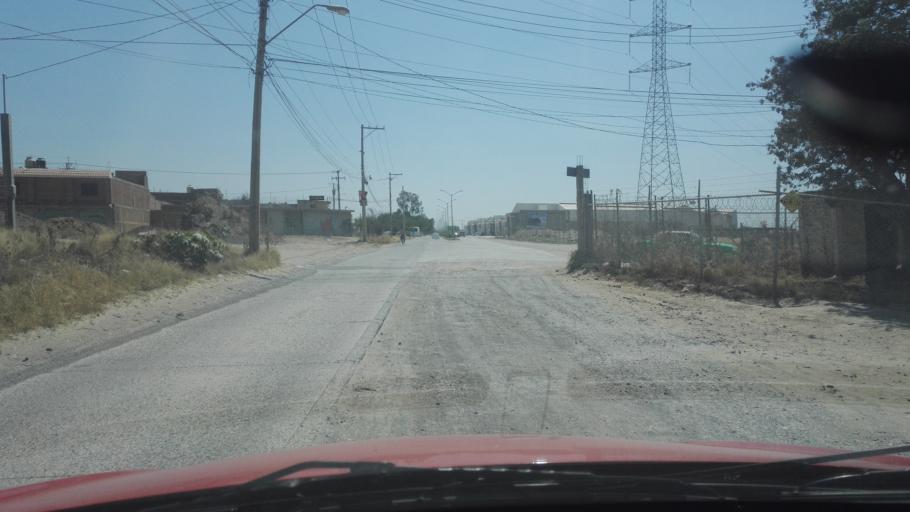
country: MX
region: Guanajuato
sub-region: Leon
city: Fraccionamiento Paraiso Real
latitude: 21.0910
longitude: -101.5961
